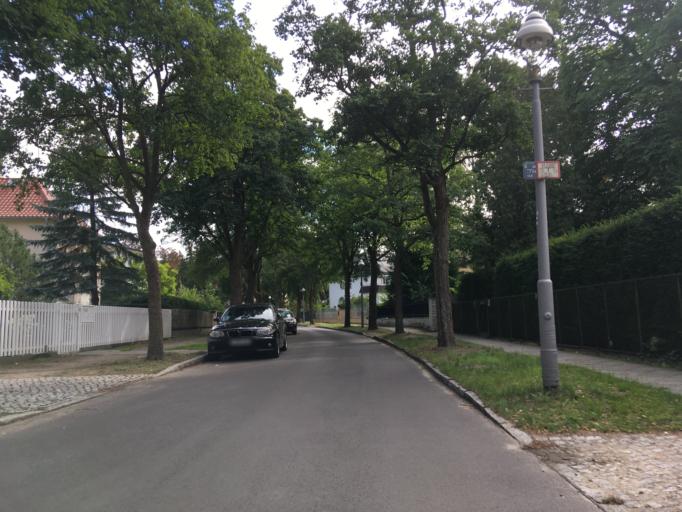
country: DE
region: Berlin
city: Frohnau
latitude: 52.6280
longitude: 13.2812
